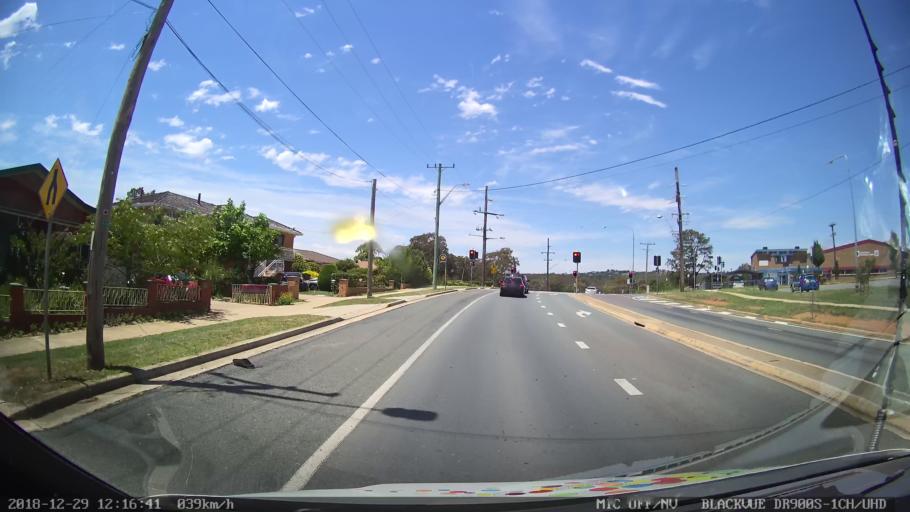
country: AU
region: New South Wales
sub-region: Queanbeyan
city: Queanbeyan
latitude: -35.3713
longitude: 149.2333
